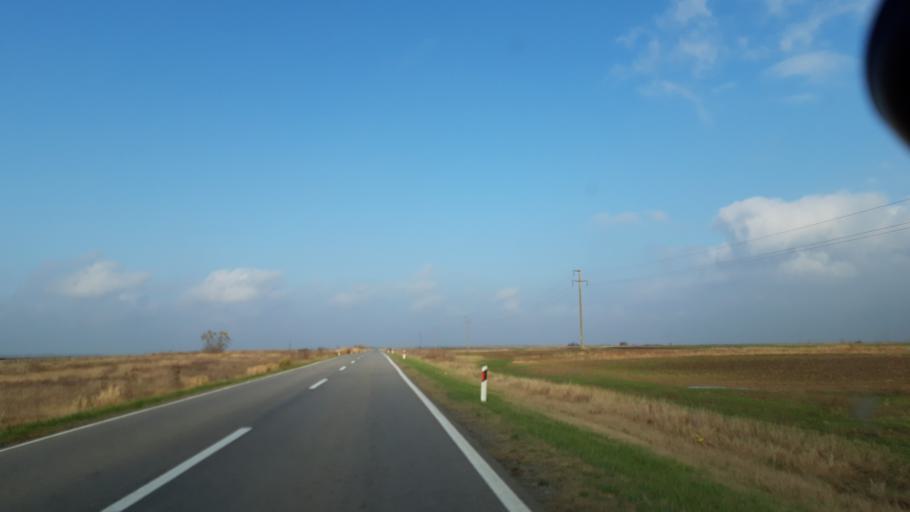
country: RS
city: Padej
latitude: 45.8423
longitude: 20.1654
